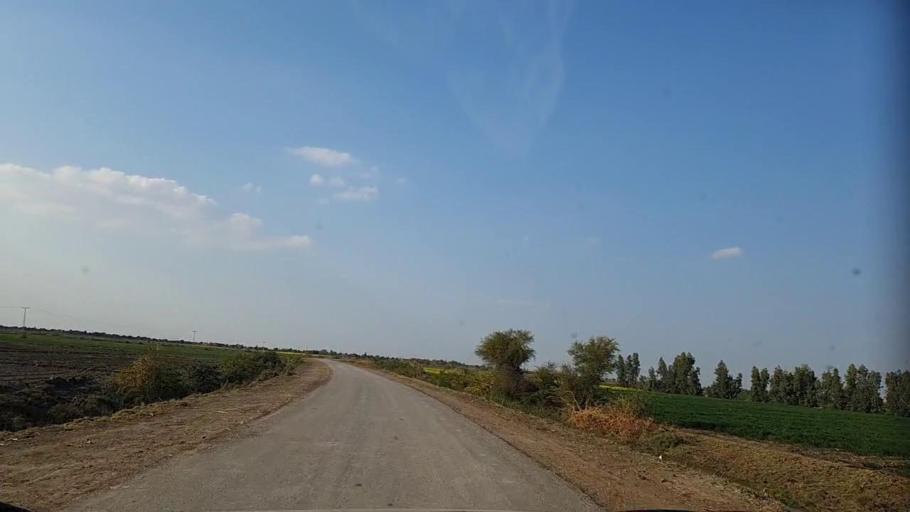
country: PK
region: Sindh
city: Pithoro
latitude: 25.7141
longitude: 69.2201
